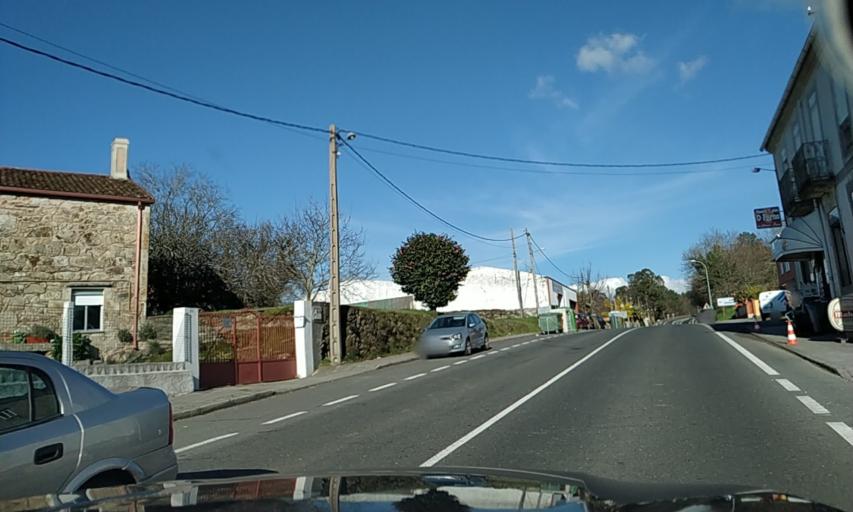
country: ES
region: Galicia
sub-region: Provincia da Coruna
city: Ribeira
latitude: 42.7060
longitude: -8.3978
